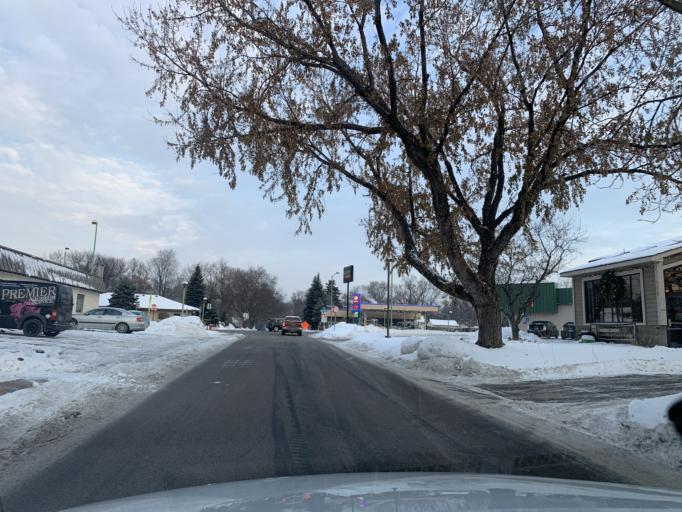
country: US
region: Minnesota
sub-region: Hennepin County
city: Saint Louis Park
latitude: 44.9286
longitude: -93.3531
